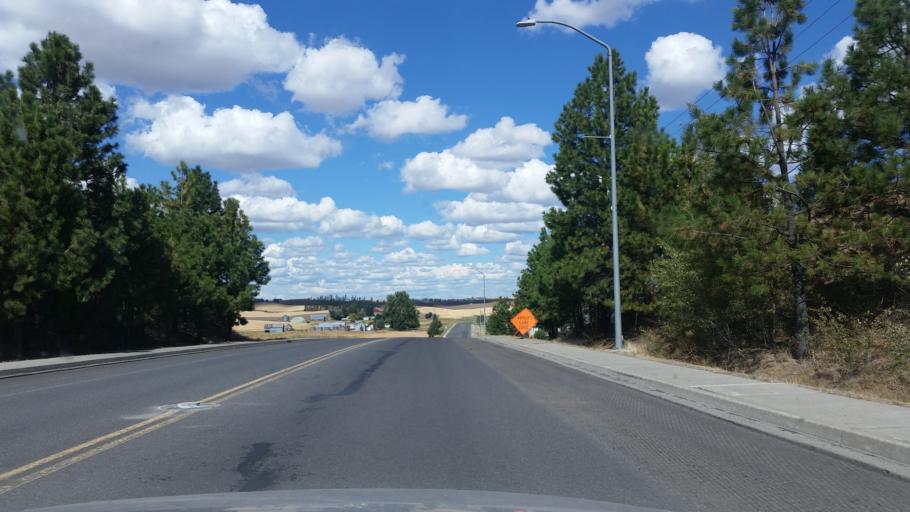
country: US
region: Washington
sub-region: Spokane County
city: Cheney
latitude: 47.4994
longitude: -117.5865
